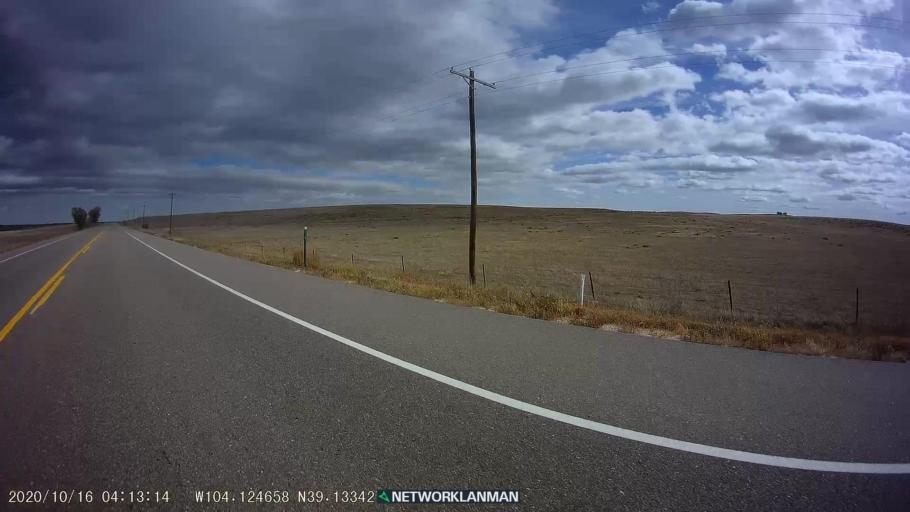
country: US
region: Colorado
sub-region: El Paso County
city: Ellicott
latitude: 39.1339
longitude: -104.1240
